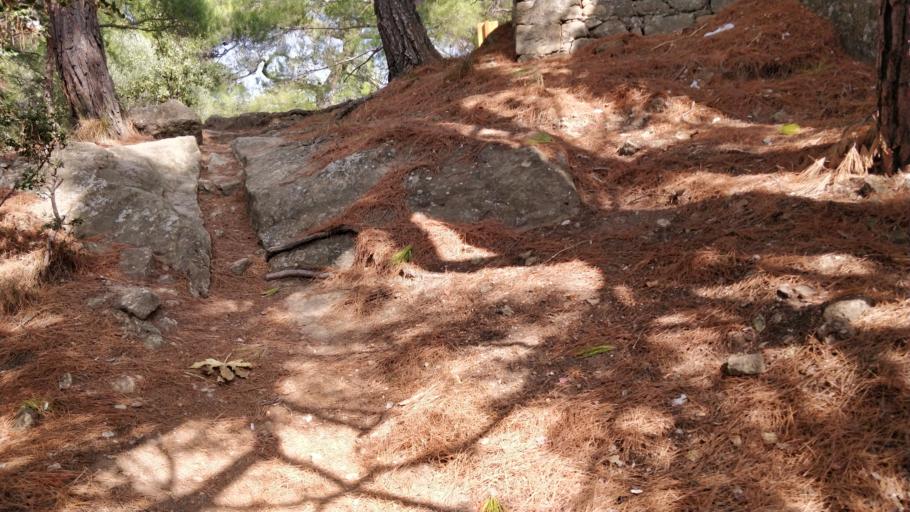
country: TR
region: Canakkale
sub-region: Merkez
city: Kucukkuyu
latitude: 39.5604
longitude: 26.6178
